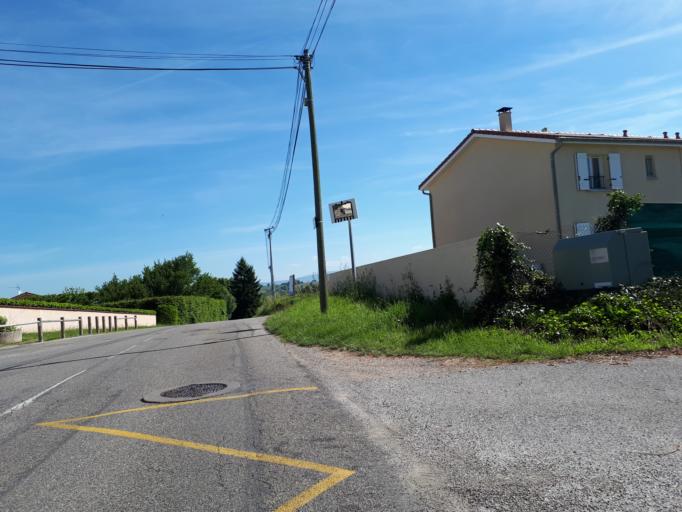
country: FR
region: Rhone-Alpes
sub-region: Departement de l'Isere
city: Saint-Savin
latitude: 45.6154
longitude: 5.3189
